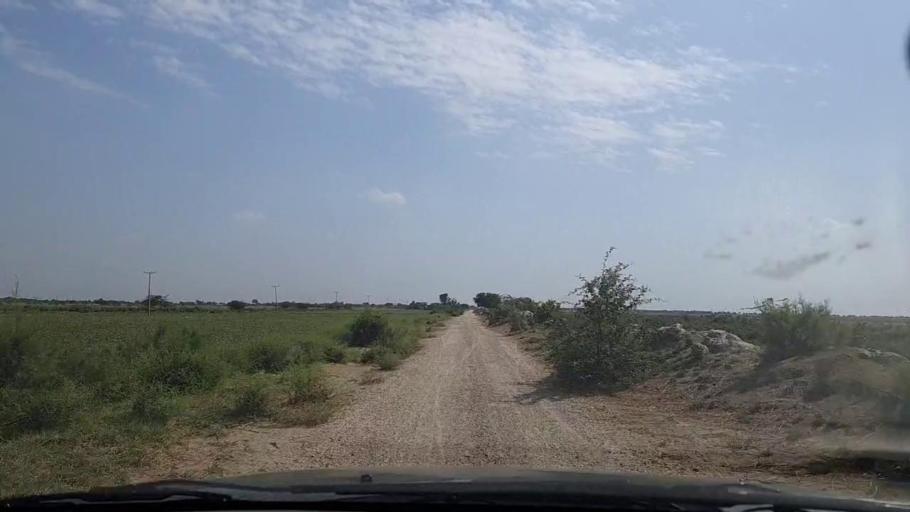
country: PK
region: Sindh
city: Mirpur Batoro
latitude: 24.5802
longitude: 68.1955
